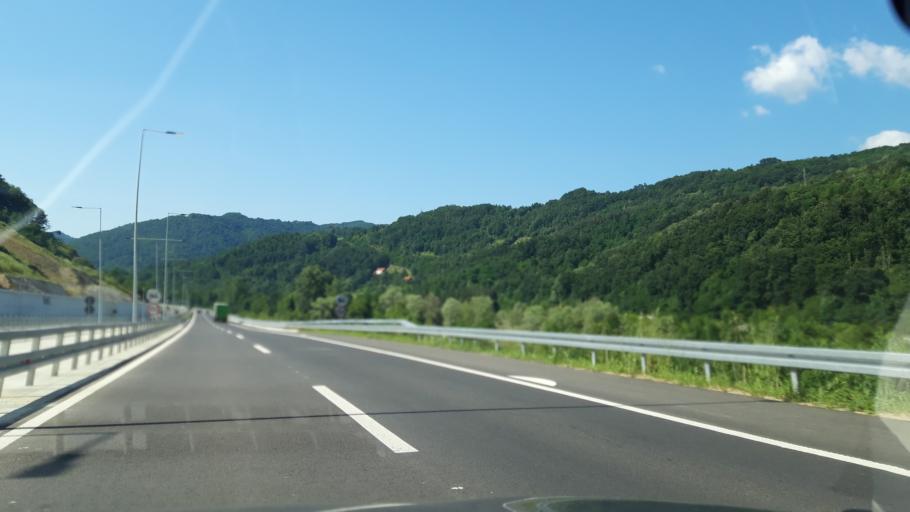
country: RS
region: Central Serbia
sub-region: Jablanicki Okrug
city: Vlasotince
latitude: 42.8449
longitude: 22.1312
